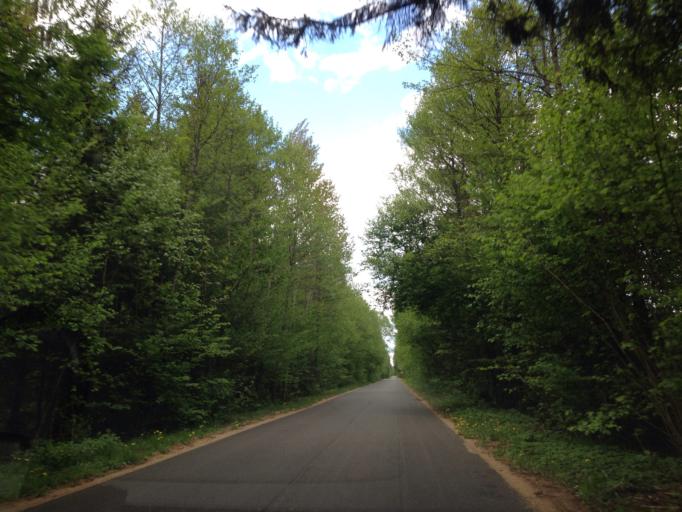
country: PL
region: Podlasie
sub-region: Powiat grajewski
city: Radzilow
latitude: 53.3274
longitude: 22.6004
